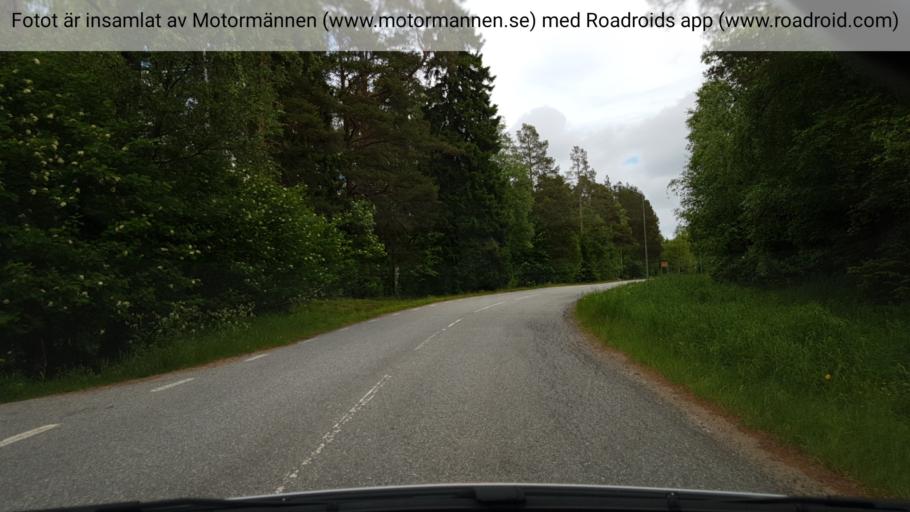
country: SE
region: Vaesterbotten
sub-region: Nordmalings Kommun
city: Nordmaling
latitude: 63.5633
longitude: 19.7016
